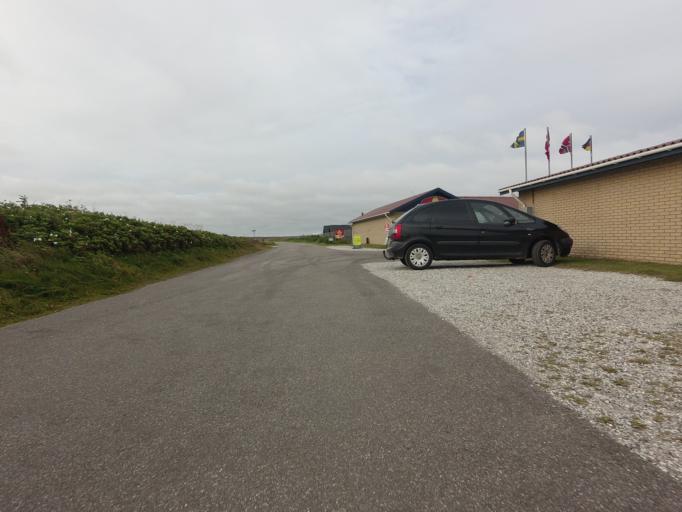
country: DK
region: North Denmark
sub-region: Jammerbugt Kommune
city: Pandrup
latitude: 57.3856
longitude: 9.7253
